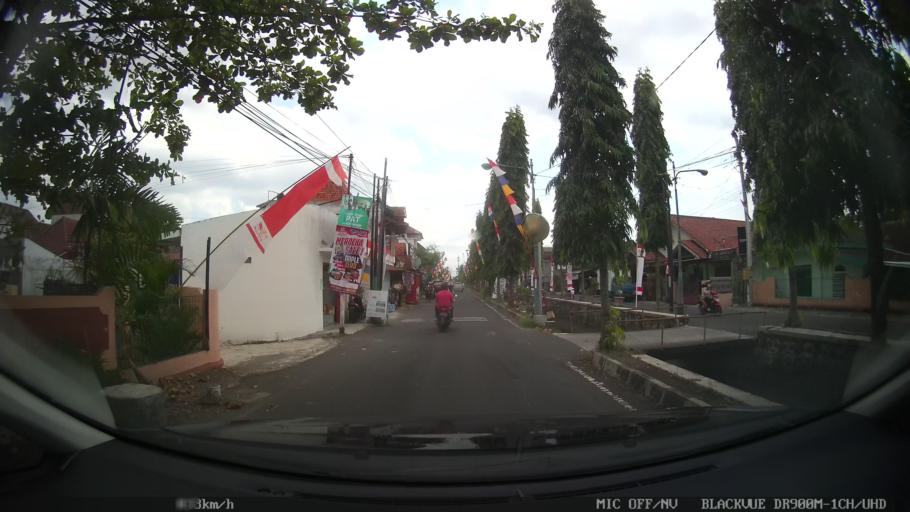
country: ID
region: Daerah Istimewa Yogyakarta
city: Yogyakarta
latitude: -7.7615
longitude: 110.3645
